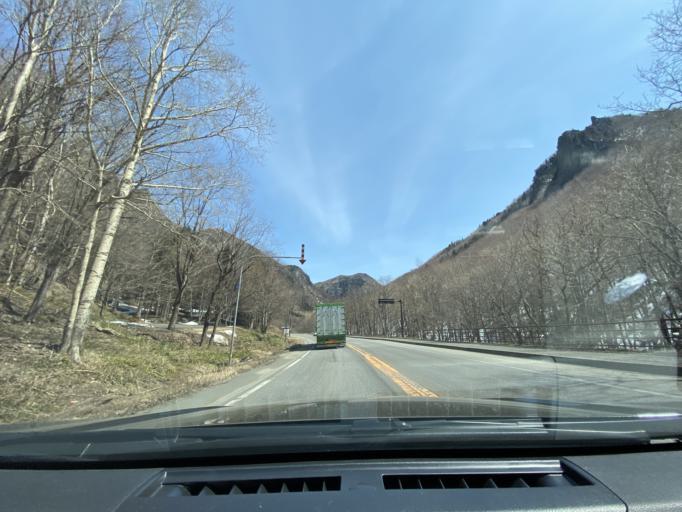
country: JP
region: Hokkaido
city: Kamikawa
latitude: 43.7258
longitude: 142.9580
